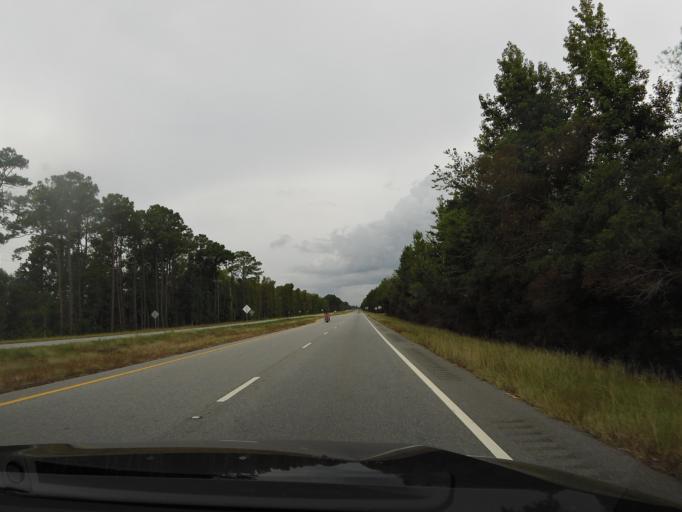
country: US
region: Georgia
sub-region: McIntosh County
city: Darien
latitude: 31.3740
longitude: -81.6280
